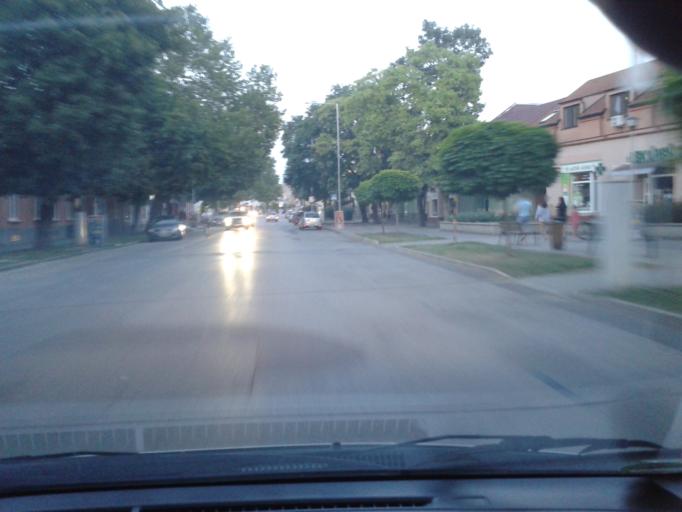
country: SK
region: Nitriansky
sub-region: Okres Nove Zamky
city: Sturovo
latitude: 47.7991
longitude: 18.7183
